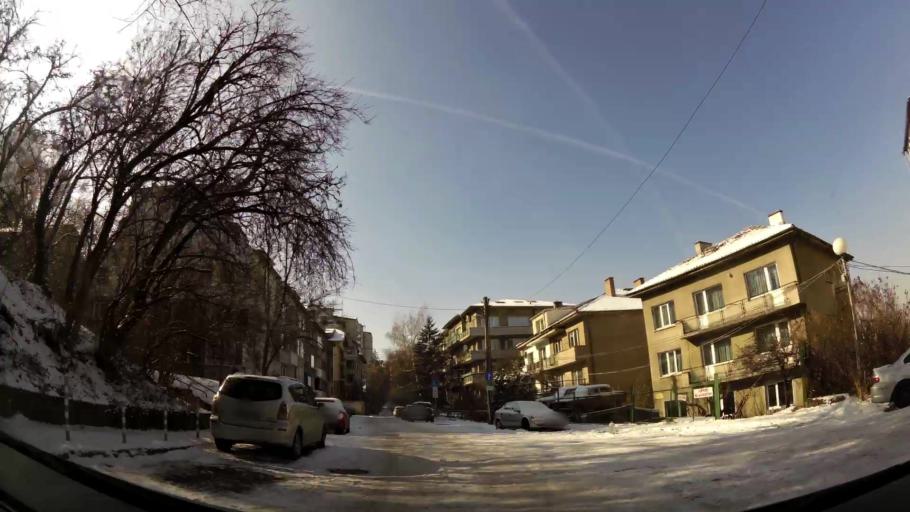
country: BG
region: Sofia-Capital
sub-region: Stolichna Obshtina
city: Sofia
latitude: 42.6743
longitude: 23.3188
